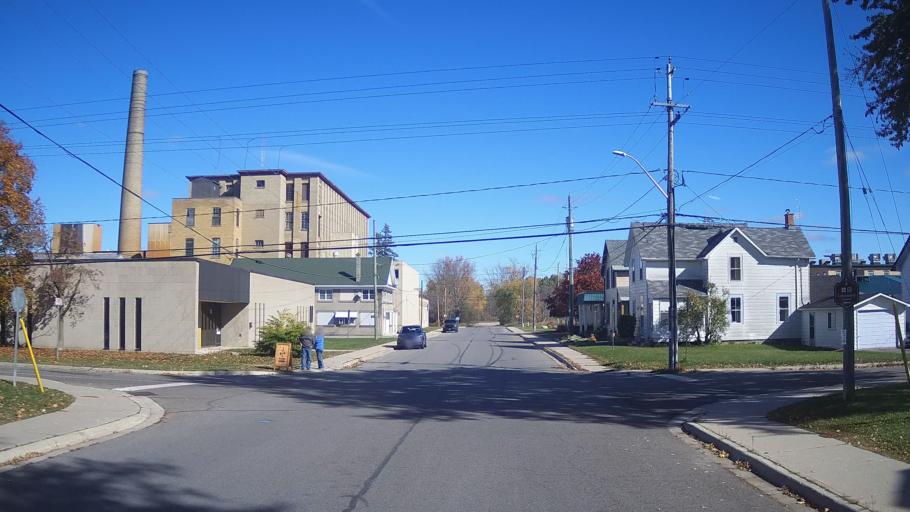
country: CA
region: Ontario
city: Perth
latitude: 44.9018
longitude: -76.2474
